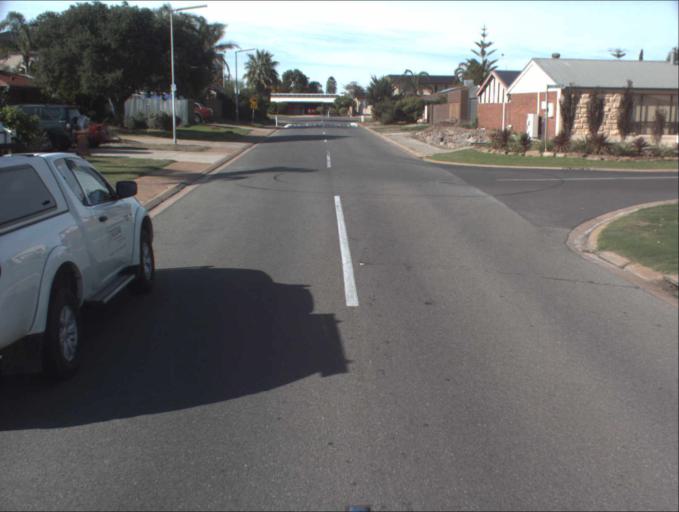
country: AU
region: South Australia
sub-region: Port Adelaide Enfield
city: Birkenhead
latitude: -34.7914
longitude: 138.4954
